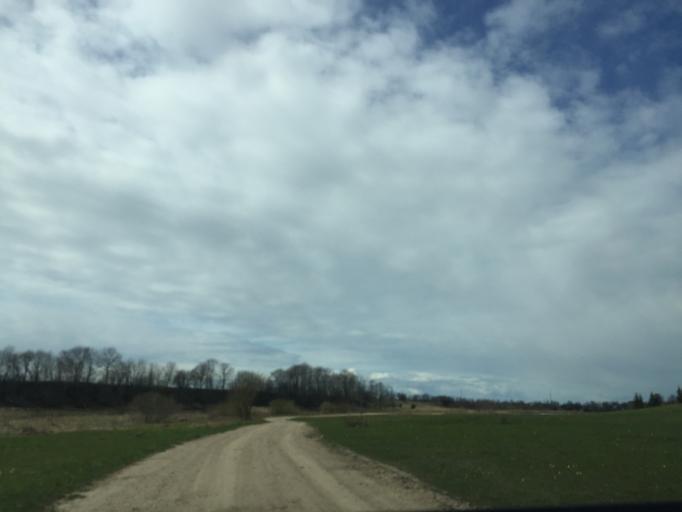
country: LV
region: Salacgrivas
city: Salacgriva
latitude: 57.7486
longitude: 24.3970
